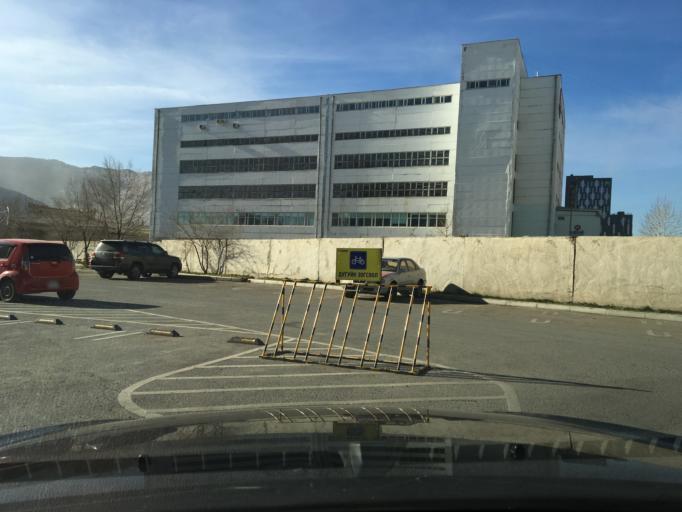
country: MN
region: Ulaanbaatar
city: Ulaanbaatar
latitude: 47.8966
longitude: 106.8884
